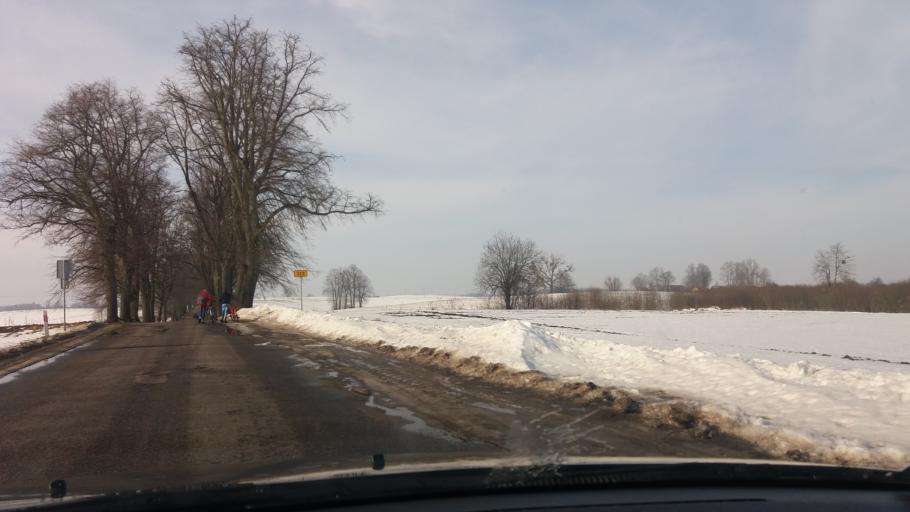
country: PL
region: Warmian-Masurian Voivodeship
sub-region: Powiat olsztynski
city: Jeziorany
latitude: 54.1006
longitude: 20.7460
